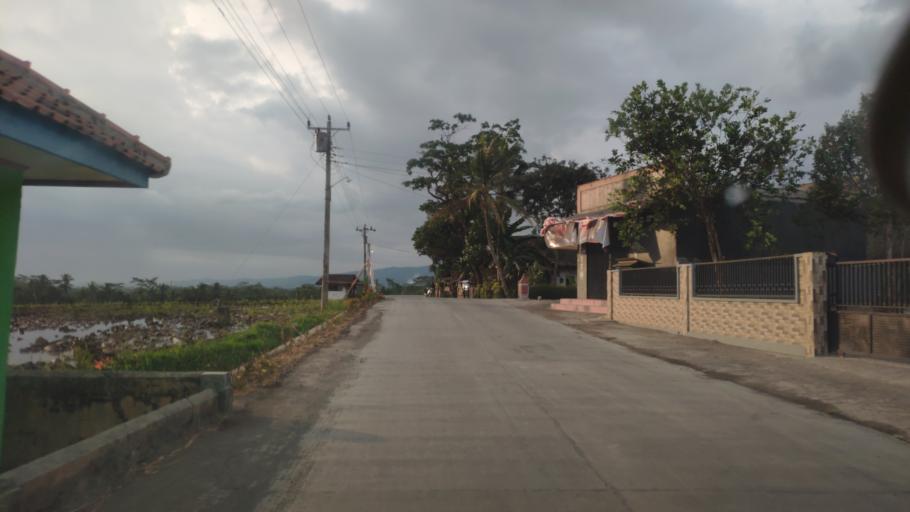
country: ID
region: Central Java
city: Wonosobo
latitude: -7.3880
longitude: 109.6676
